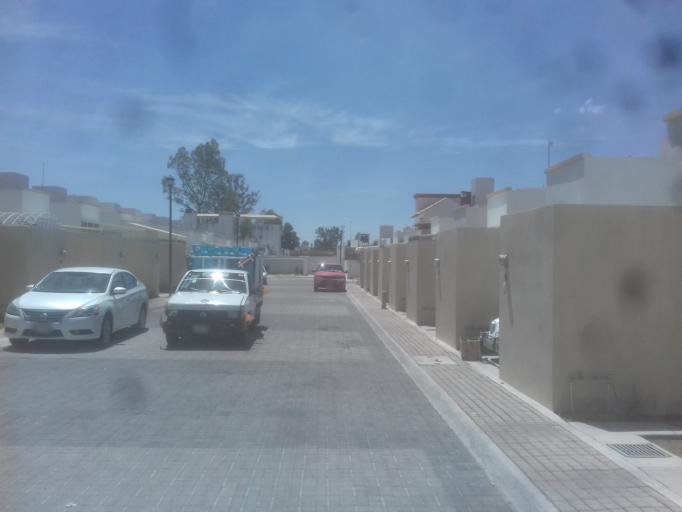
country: MX
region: Aguascalientes
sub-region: Aguascalientes
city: San Sebastian [Fraccionamiento]
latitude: 21.8111
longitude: -102.3011
